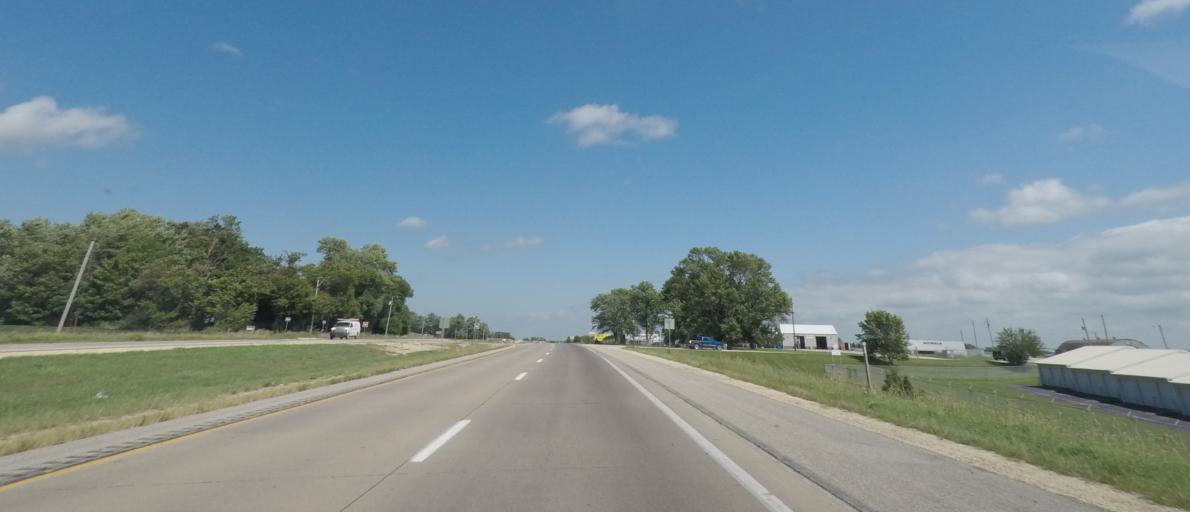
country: US
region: Iowa
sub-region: Linn County
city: Marion
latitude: 42.0362
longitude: -91.5365
